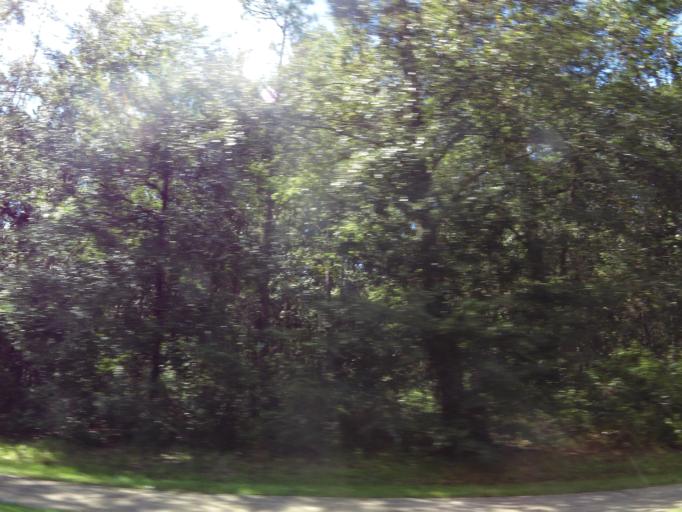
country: US
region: Florida
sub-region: Union County
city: Lake Butler
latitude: 30.0200
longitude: -82.3322
